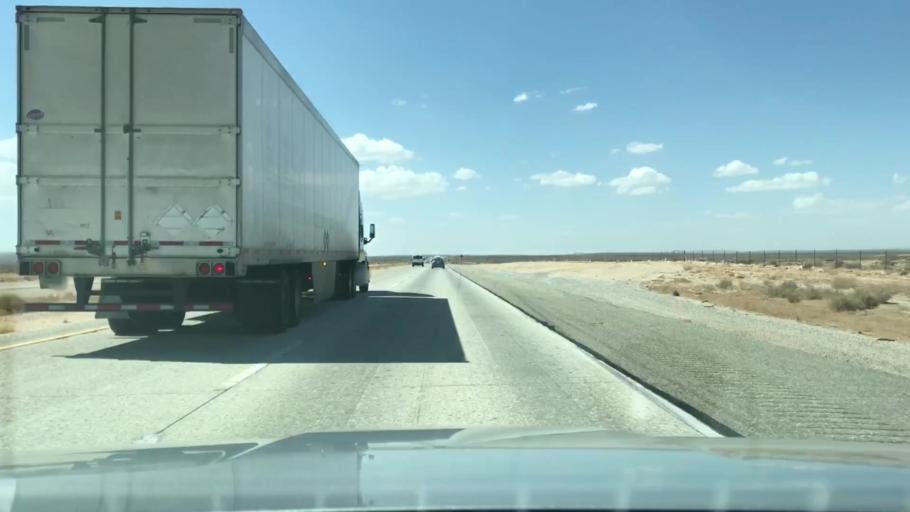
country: US
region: California
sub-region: San Bernardino County
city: Lenwood
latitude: 34.9273
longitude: -117.3486
